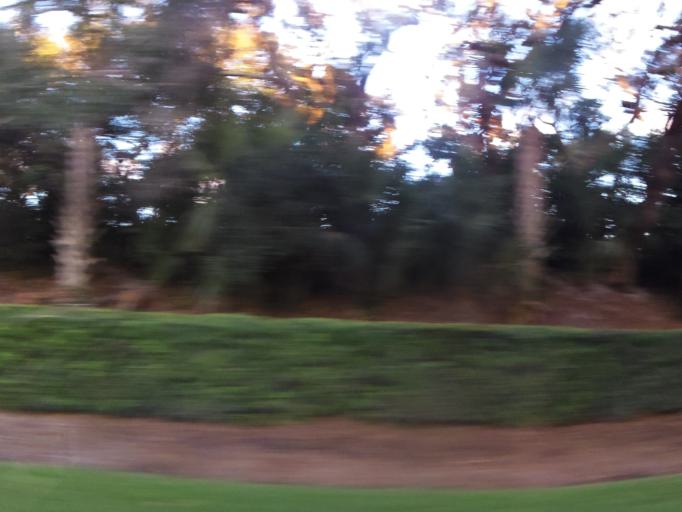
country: US
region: Florida
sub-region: Saint Johns County
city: Sawgrass
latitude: 30.1762
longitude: -81.3609
